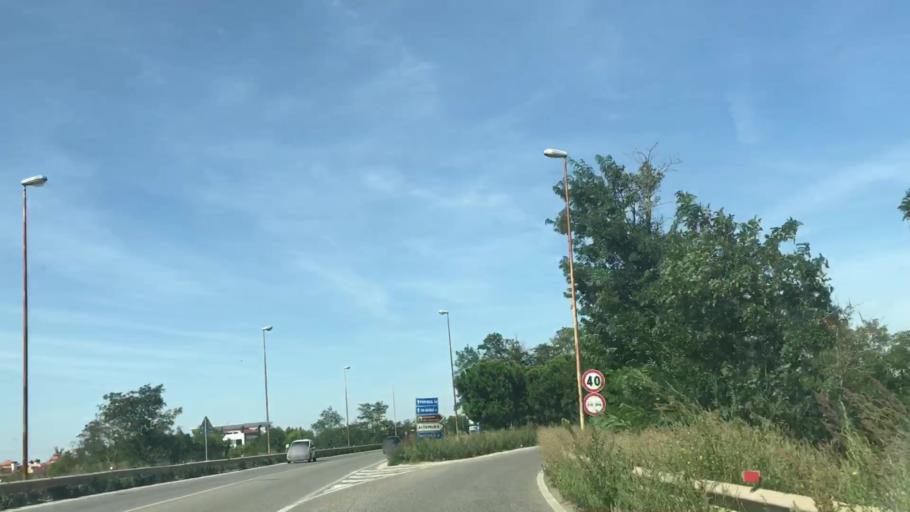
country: IT
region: Apulia
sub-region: Provincia di Bari
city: Altamura
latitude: 40.8145
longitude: 16.5569
